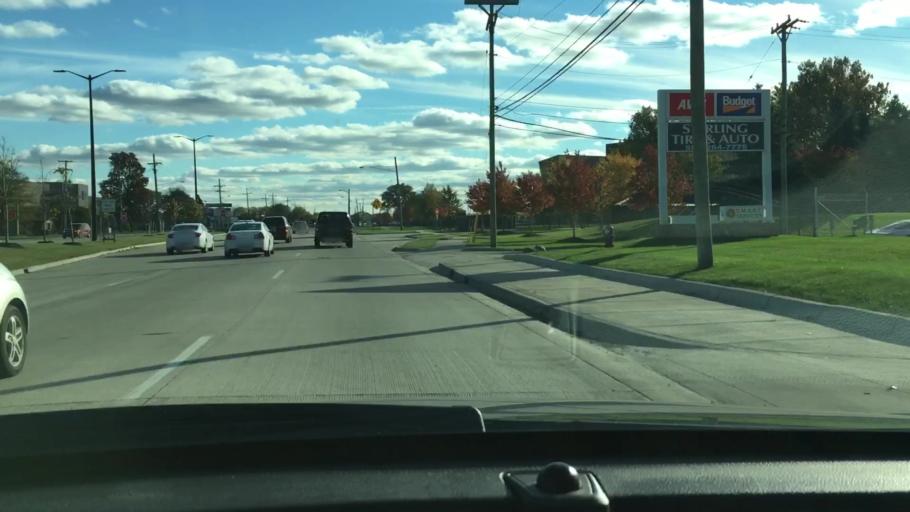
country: US
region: Michigan
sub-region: Macomb County
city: Sterling Heights
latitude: 42.5490
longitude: -83.0291
